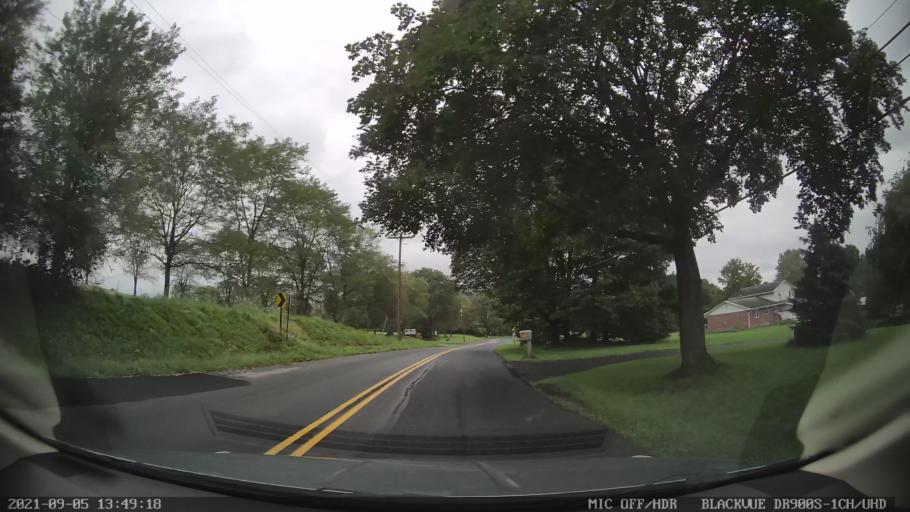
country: US
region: Pennsylvania
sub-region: Lehigh County
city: Schnecksville
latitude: 40.6293
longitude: -75.5753
